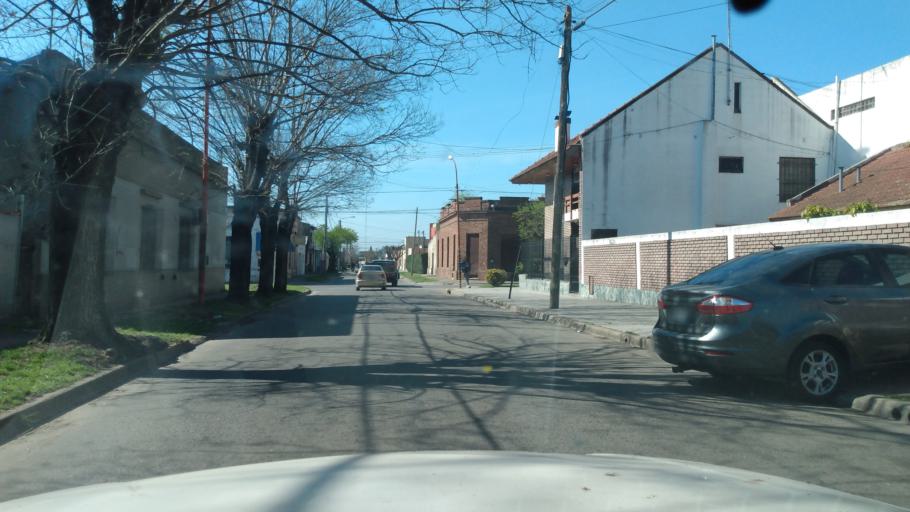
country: AR
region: Buenos Aires
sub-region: Partido de Lujan
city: Lujan
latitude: -34.5707
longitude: -59.0999
